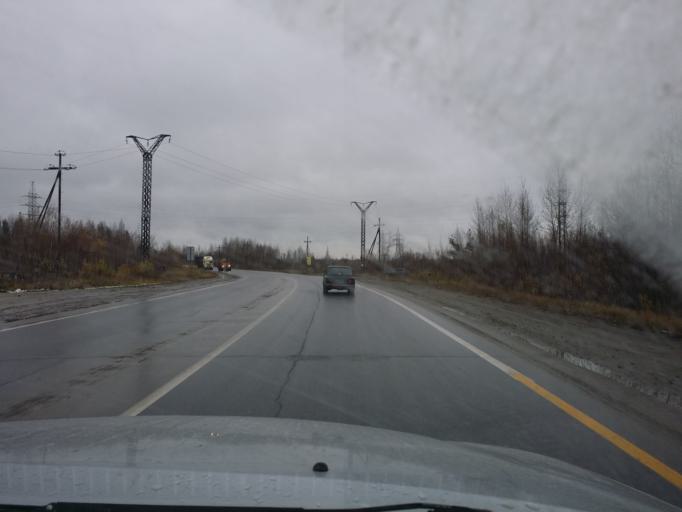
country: RU
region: Khanty-Mansiyskiy Avtonomnyy Okrug
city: Megion
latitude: 61.0827
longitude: 76.1175
